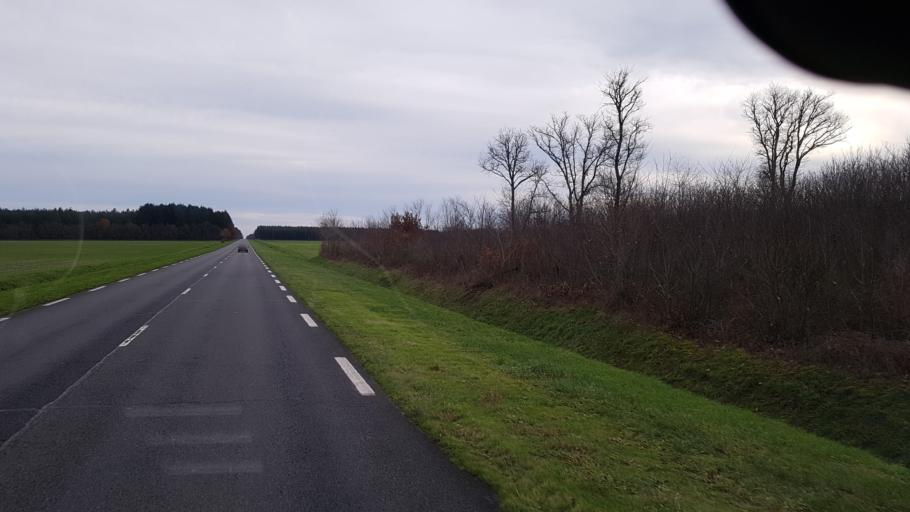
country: FR
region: Centre
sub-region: Departement du Loir-et-Cher
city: Lamotte-Beuvron
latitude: 47.6431
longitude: 1.9950
